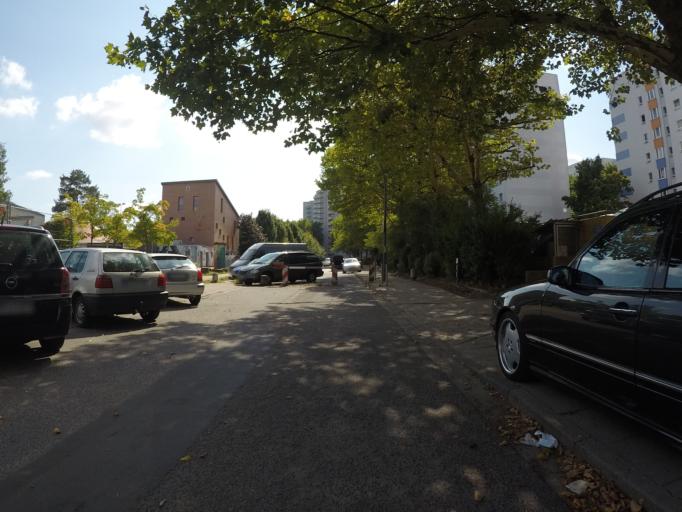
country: DE
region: Hamburg
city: Stellingen
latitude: 53.5852
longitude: 9.9501
